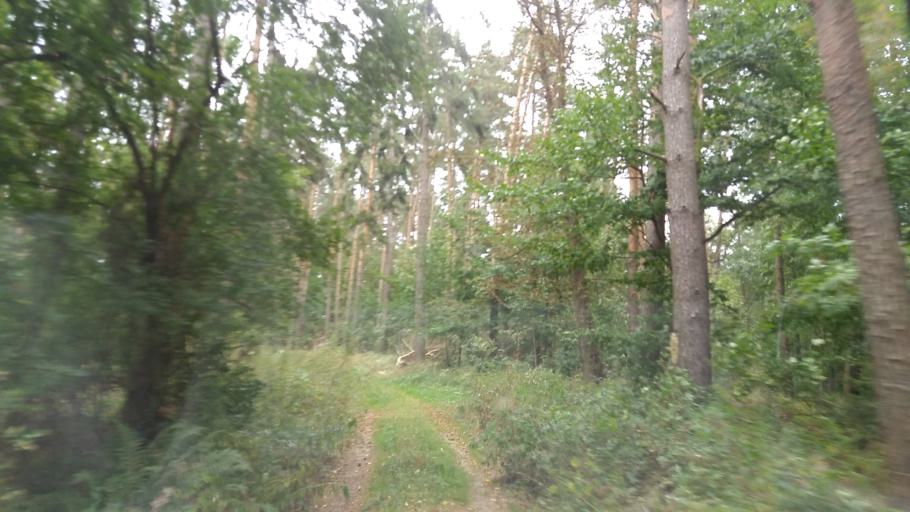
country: PL
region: West Pomeranian Voivodeship
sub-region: Powiat choszczenski
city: Bierzwnik
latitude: 52.9903
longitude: 15.6074
